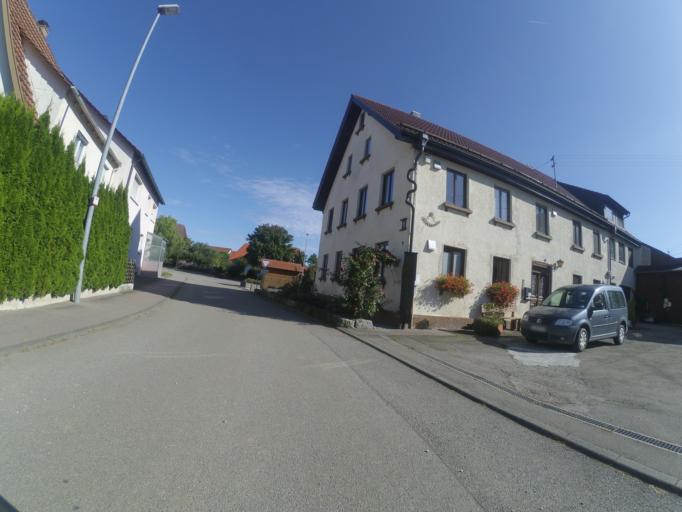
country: DE
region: Baden-Wuerttemberg
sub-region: Tuebingen Region
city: Holzkirch
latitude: 48.5308
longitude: 9.9960
